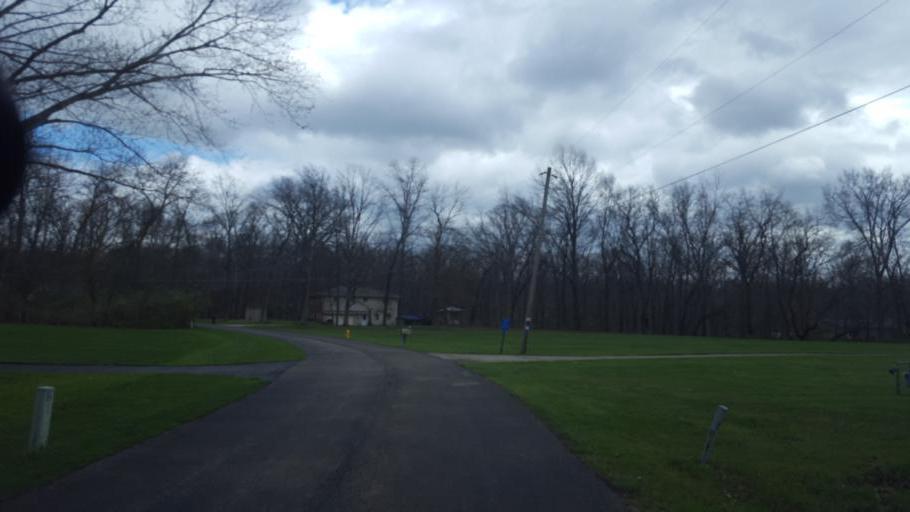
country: US
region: Ohio
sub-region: Franklin County
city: Westerville
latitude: 40.1415
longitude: -82.8712
